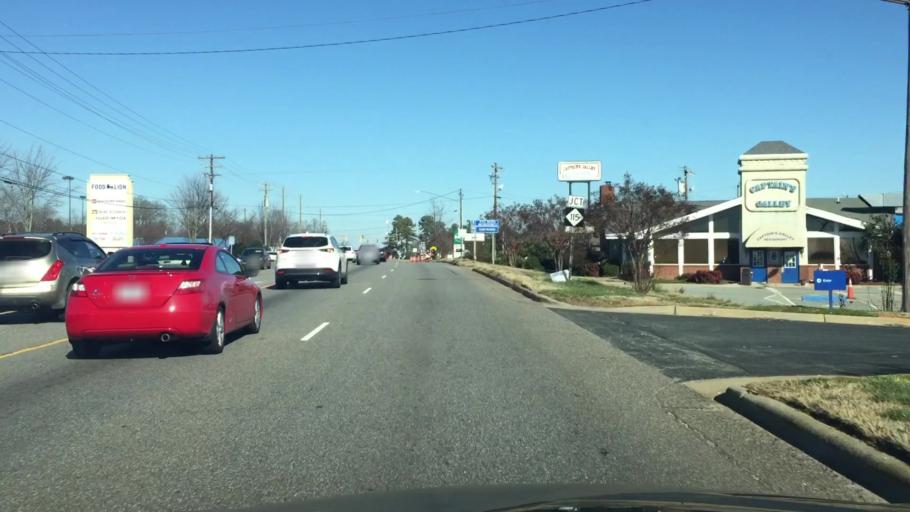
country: US
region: North Carolina
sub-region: Iredell County
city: Mooresville
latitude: 35.5988
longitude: -80.8128
